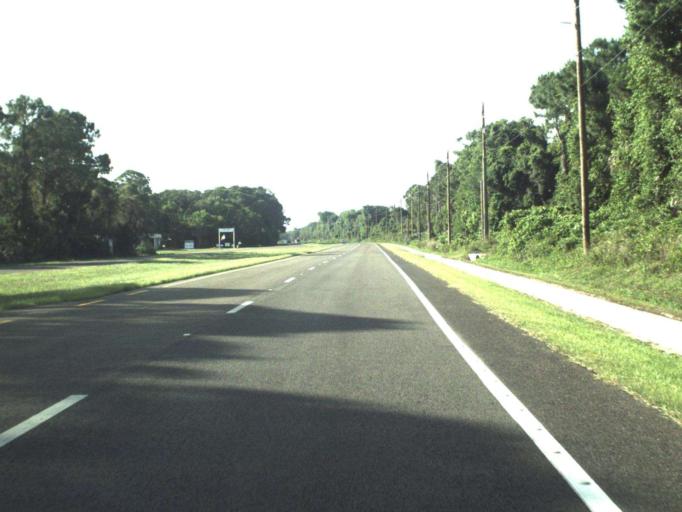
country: US
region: Florida
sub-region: Volusia County
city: Oak Hill
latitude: 28.8494
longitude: -80.8482
